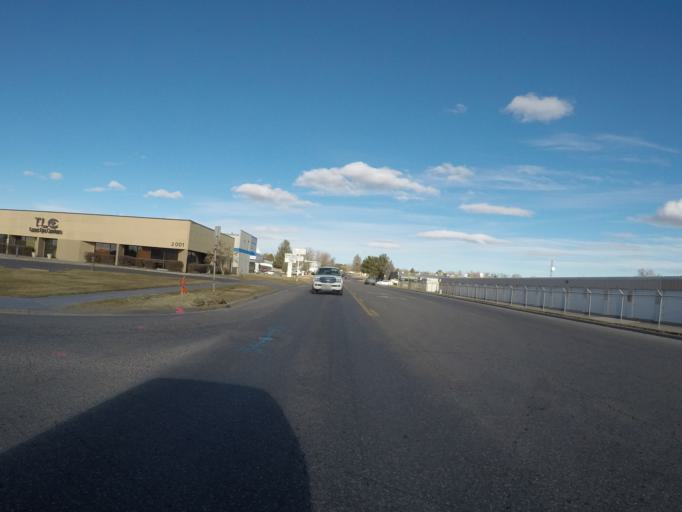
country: US
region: Montana
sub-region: Yellowstone County
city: Billings
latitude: 45.7588
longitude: -108.5667
